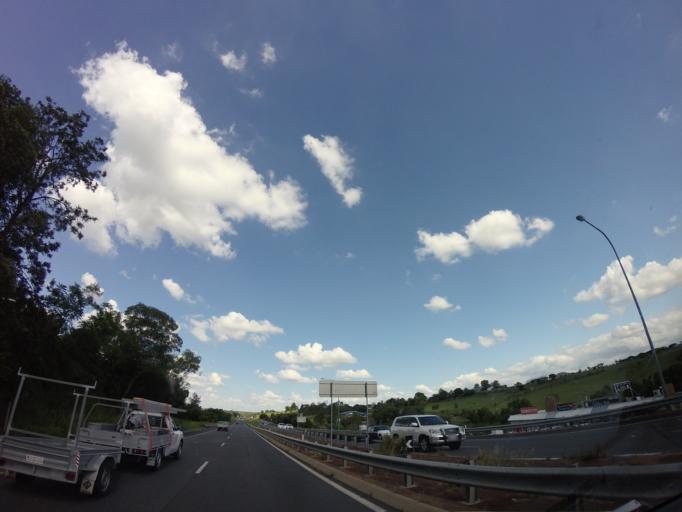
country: AU
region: Queensland
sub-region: Ipswich
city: Thagoona
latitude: -27.5631
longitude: 152.5824
